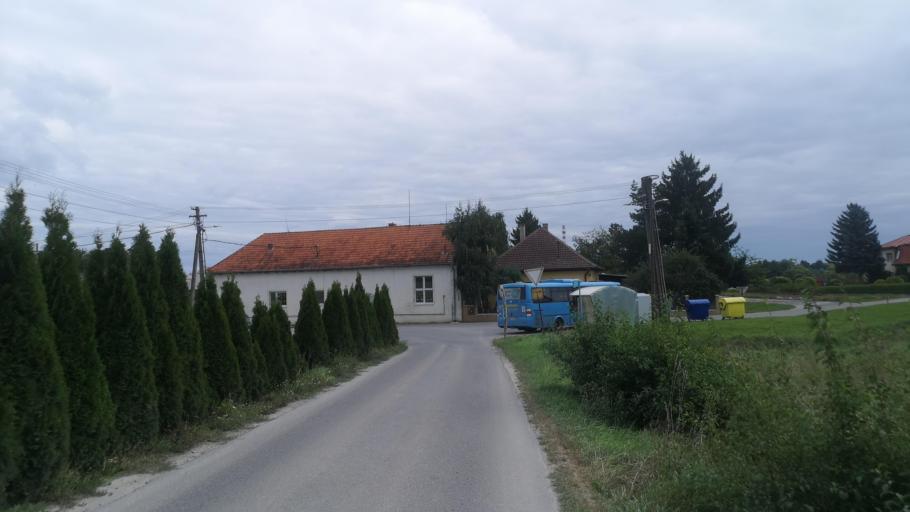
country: SK
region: Nitriansky
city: Banovce nad Bebravou
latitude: 48.7368
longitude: 18.2340
